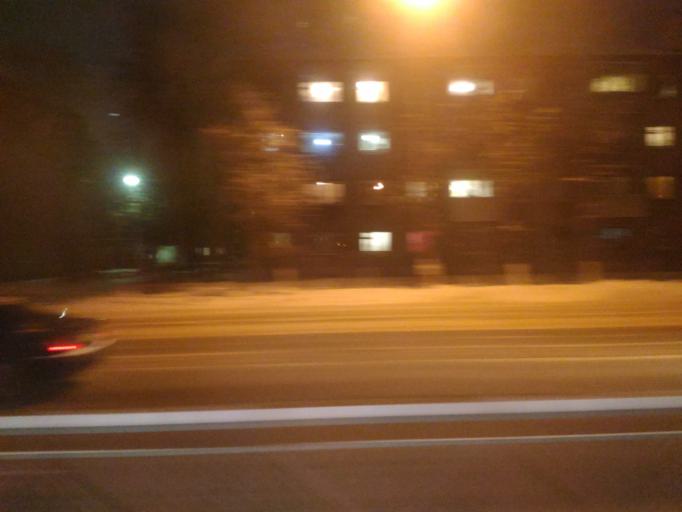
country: RU
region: Ulyanovsk
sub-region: Ulyanovskiy Rayon
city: Ulyanovsk
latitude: 54.3435
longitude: 48.3758
